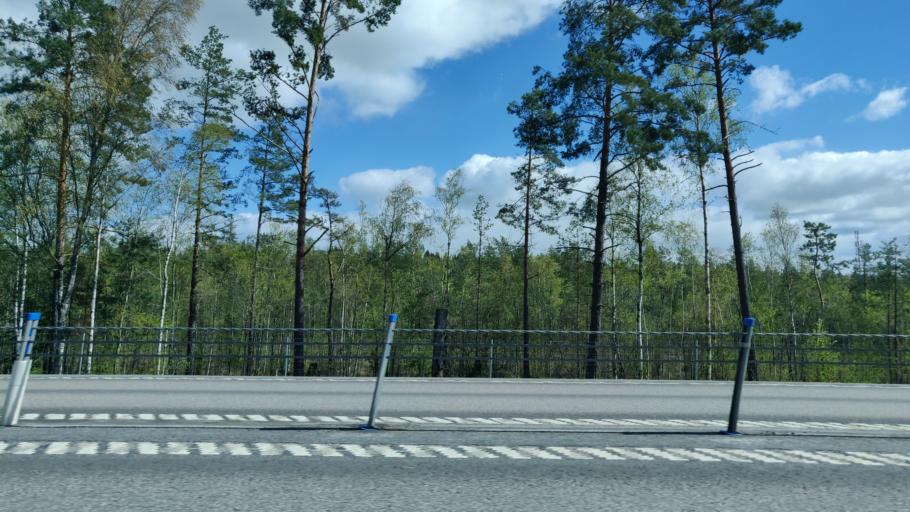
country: SE
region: Vaermland
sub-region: Karlstads Kommun
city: Karlstad
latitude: 59.4149
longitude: 13.5324
